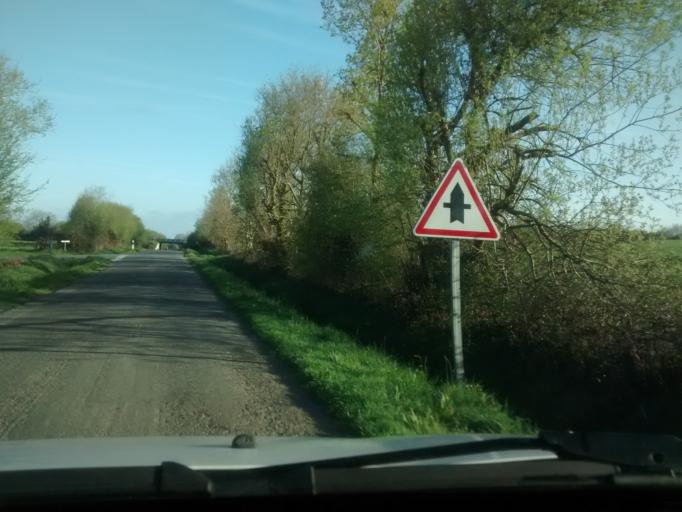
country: FR
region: Brittany
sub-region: Departement d'Ille-et-Vilaine
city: Saint-Broladre
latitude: 48.5615
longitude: -1.6385
